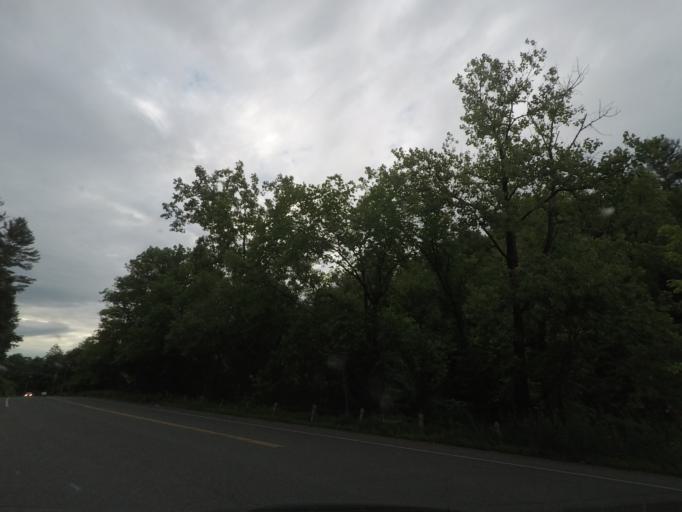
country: US
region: Connecticut
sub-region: Litchfield County
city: Canaan
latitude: 41.9346
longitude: -73.3914
